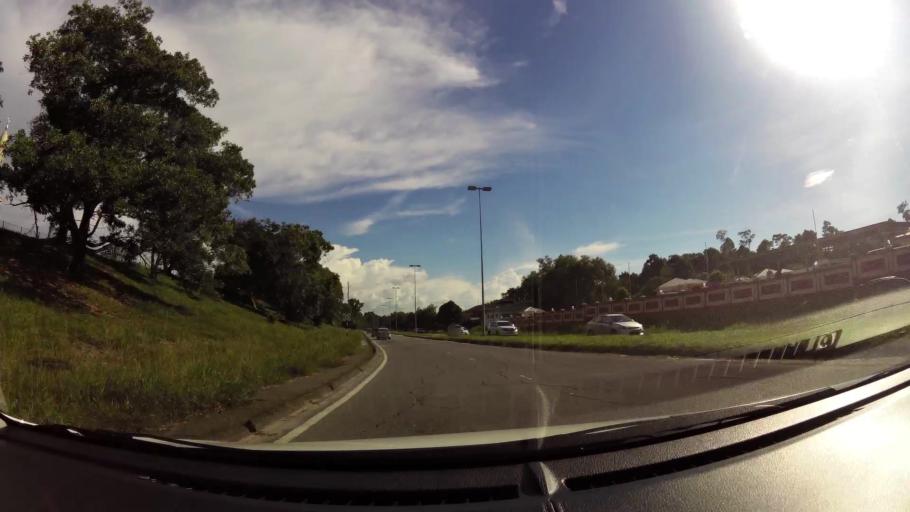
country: BN
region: Brunei and Muara
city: Bandar Seri Begawan
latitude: 4.9717
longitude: 114.9661
